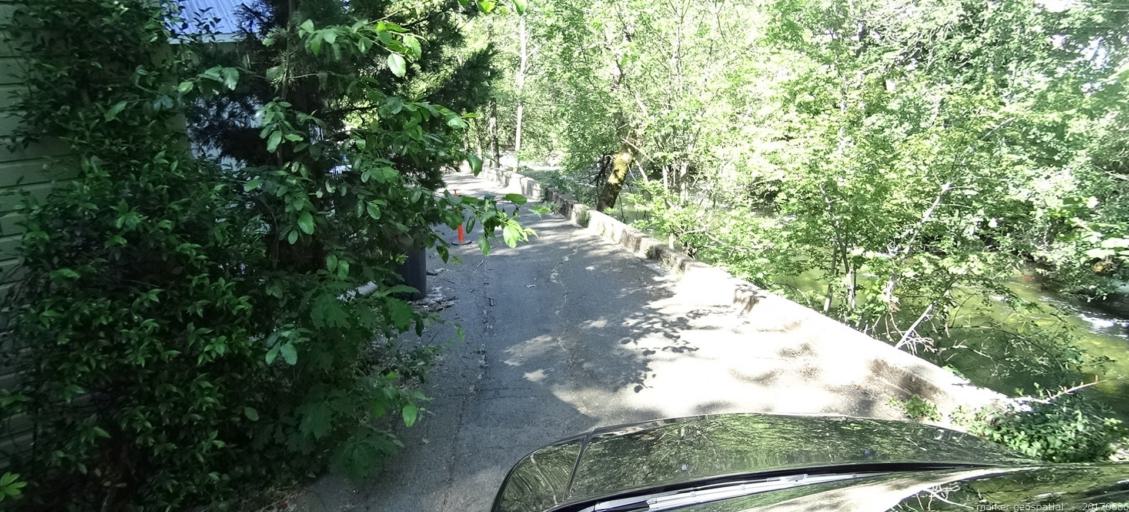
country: US
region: California
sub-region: Siskiyou County
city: Dunsmuir
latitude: 41.2093
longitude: -122.2702
